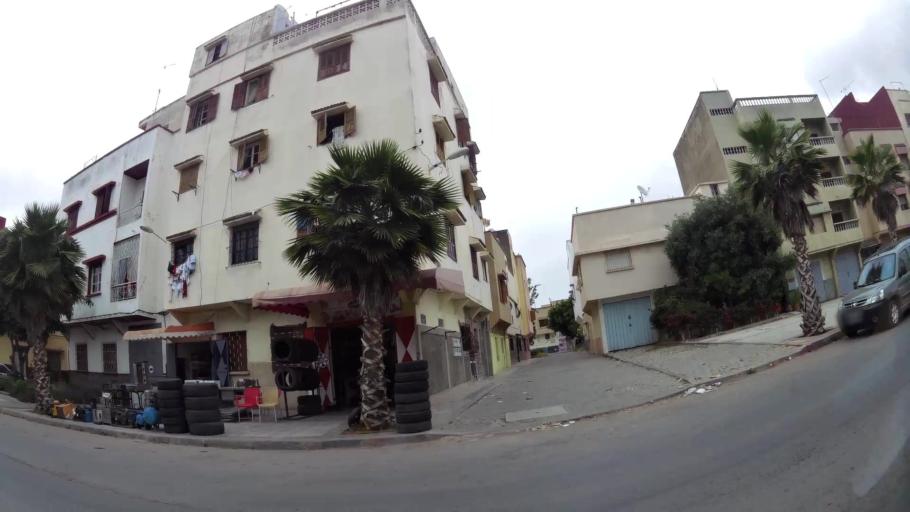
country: MA
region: Rabat-Sale-Zemmour-Zaer
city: Sale
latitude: 34.0435
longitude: -6.7983
